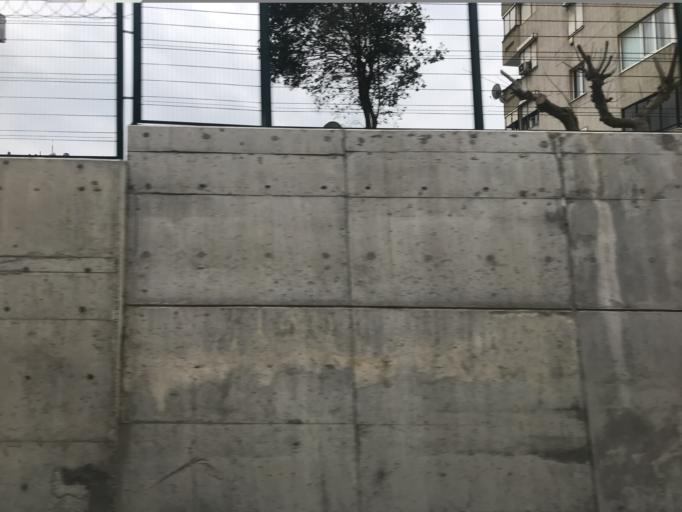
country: TR
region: Istanbul
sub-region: Atasehir
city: Atasehir
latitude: 40.9599
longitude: 29.0876
